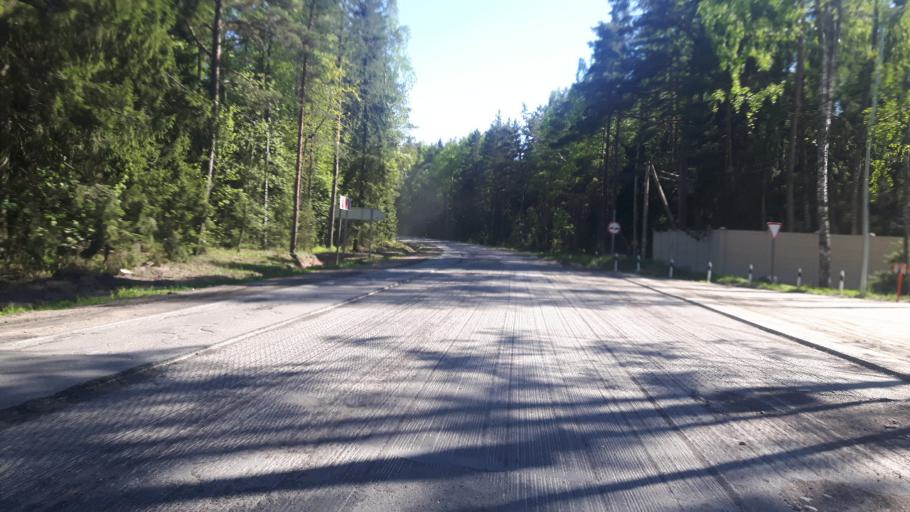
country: RU
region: Leningrad
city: Sosnovyy Bor
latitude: 60.2300
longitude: 29.0021
